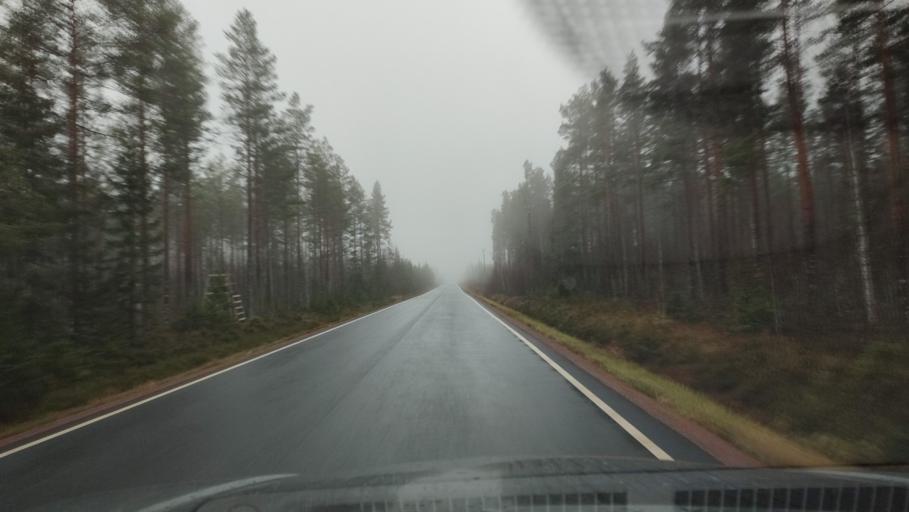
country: FI
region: Southern Ostrobothnia
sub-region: Suupohja
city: Karijoki
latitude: 62.1648
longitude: 21.7375
